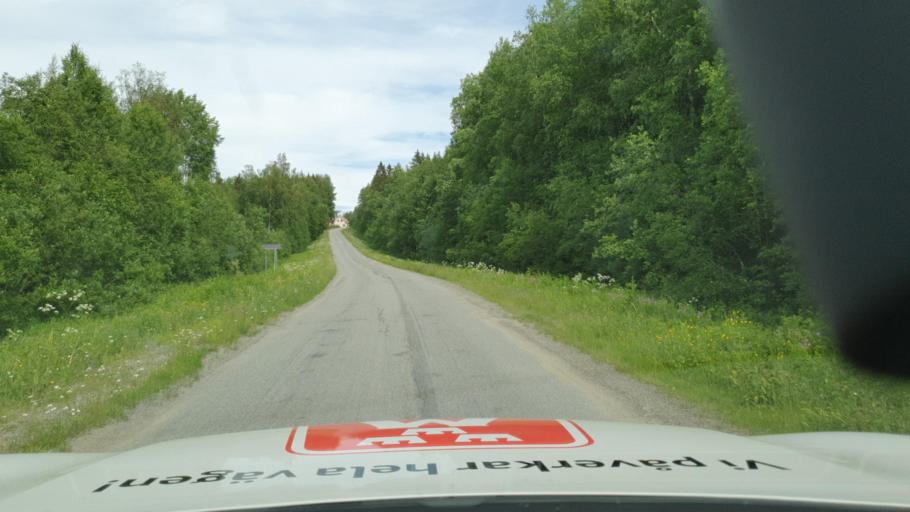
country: SE
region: Vaesterbotten
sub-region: Skelleftea Kommun
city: Burtraesk
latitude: 64.4827
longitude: 20.5301
